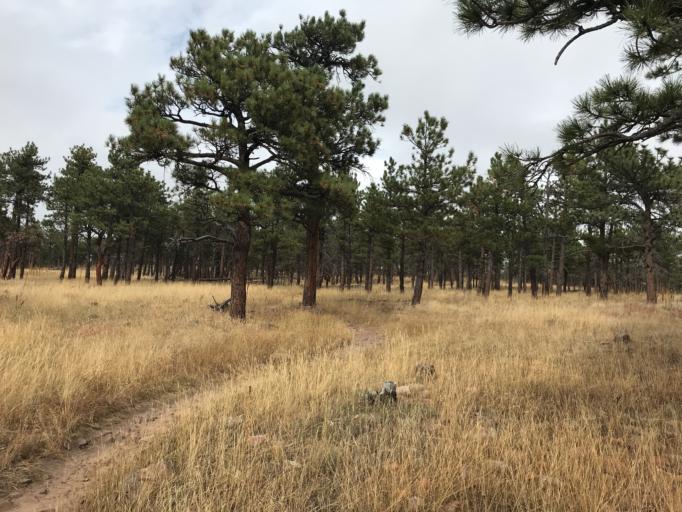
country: US
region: Colorado
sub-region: Boulder County
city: Lyons
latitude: 40.1735
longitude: -105.2996
